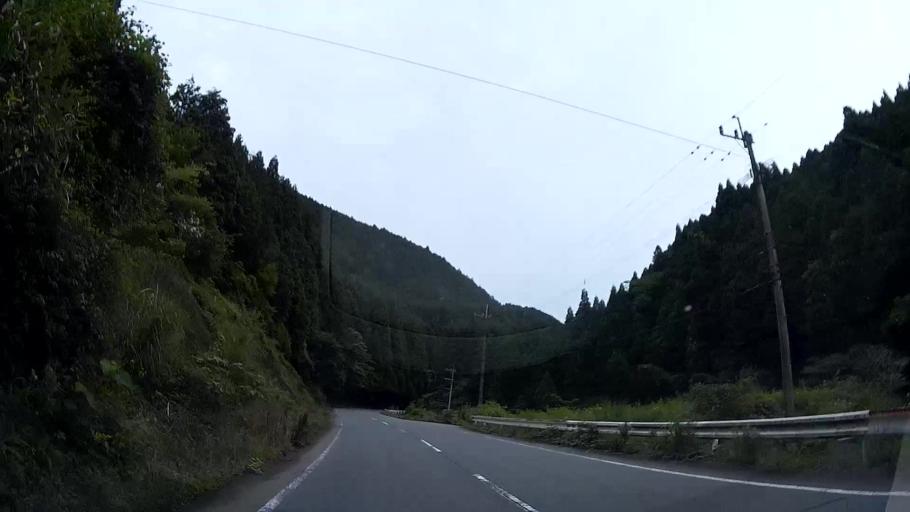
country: JP
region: Kumamoto
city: Kikuchi
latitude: 33.0485
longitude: 130.8960
